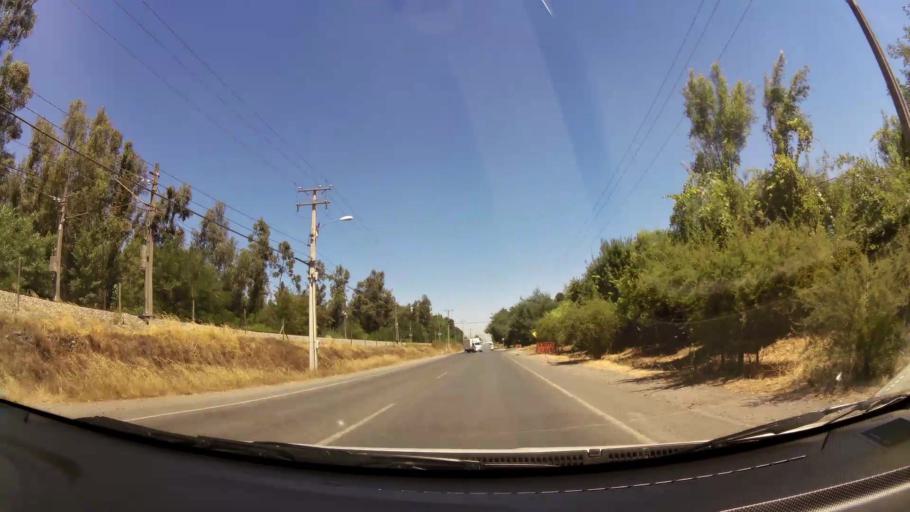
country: CL
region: O'Higgins
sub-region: Provincia de Cachapoal
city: Rancagua
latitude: -34.2342
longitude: -70.7885
